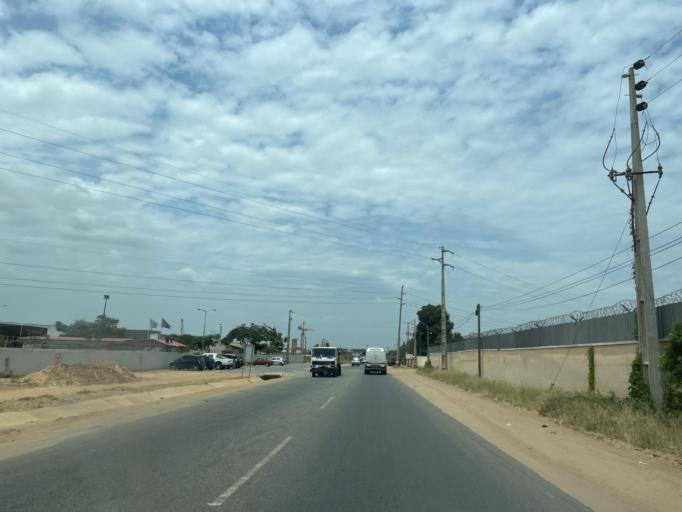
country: AO
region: Luanda
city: Luanda
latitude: -8.9340
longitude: 13.3919
